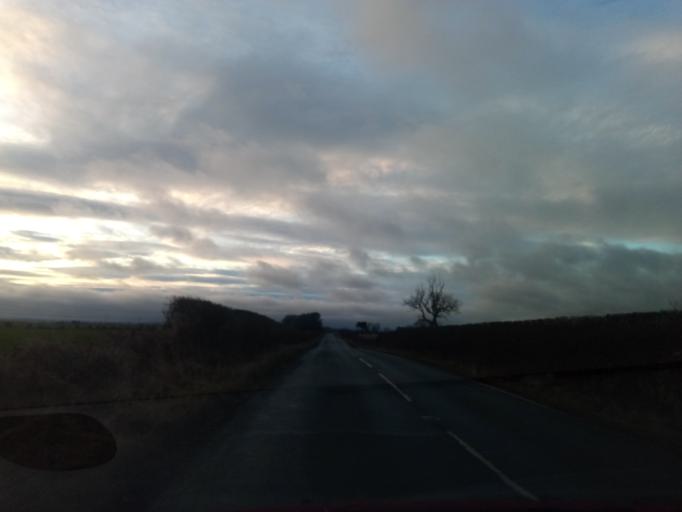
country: GB
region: England
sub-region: Northumberland
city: Morpeth
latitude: 55.1409
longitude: -1.7348
